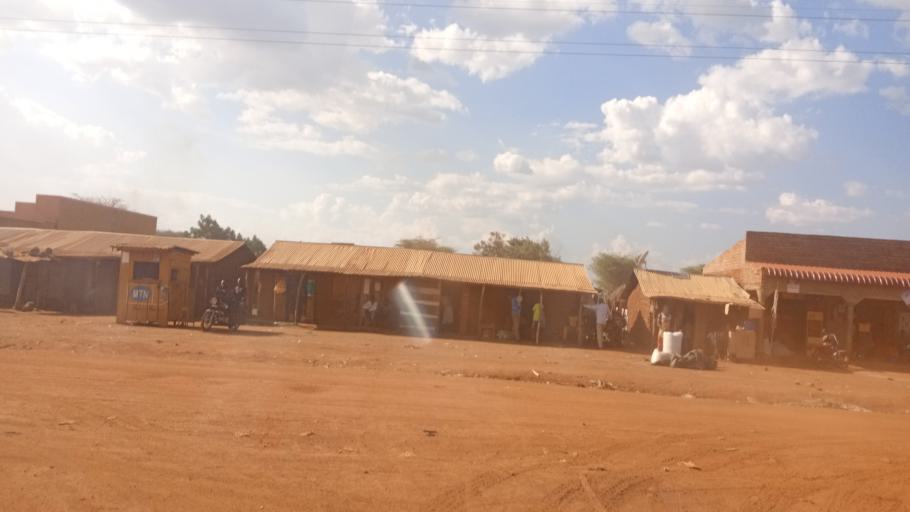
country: UG
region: Eastern Region
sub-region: Kween District
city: Binyin
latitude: 1.5257
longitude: 34.4895
